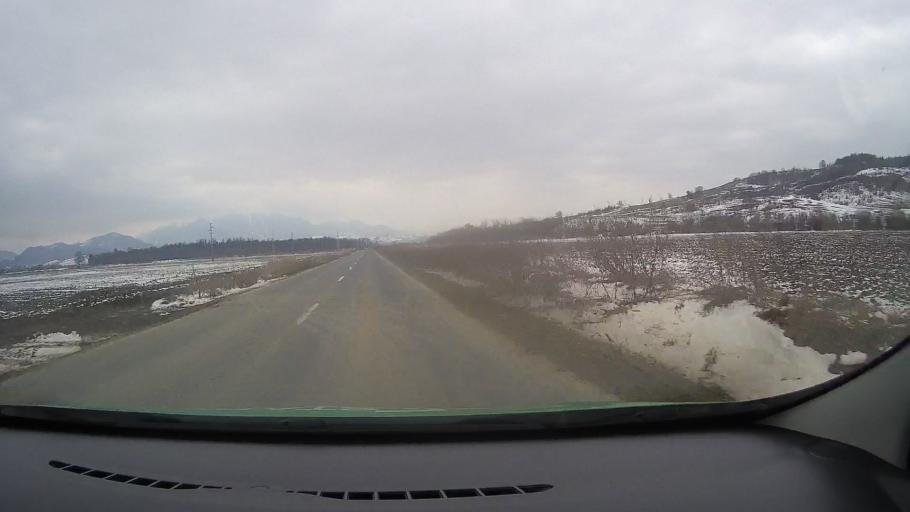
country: RO
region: Brasov
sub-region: Comuna Vulcan
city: Vulcan
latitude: 45.6041
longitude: 25.4209
